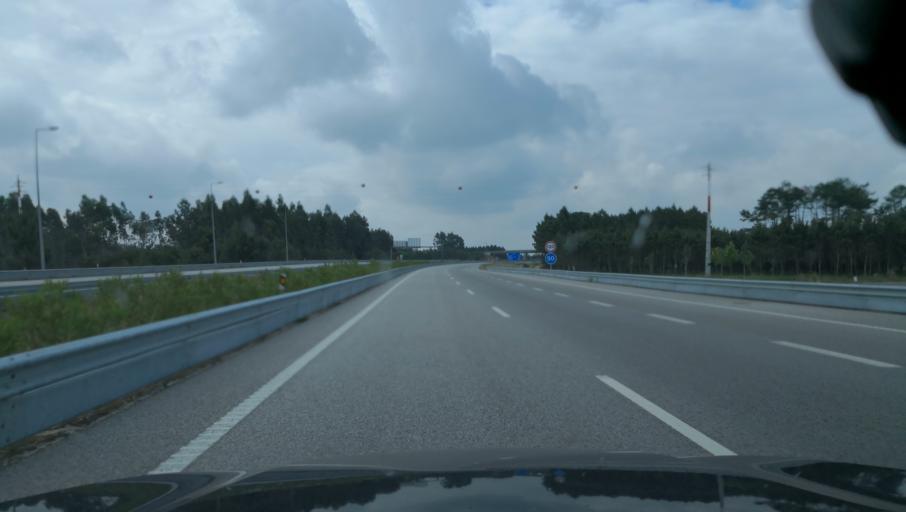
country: PT
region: Coimbra
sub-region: Montemor-O-Velho
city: Arazede
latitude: 40.3235
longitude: -8.7214
